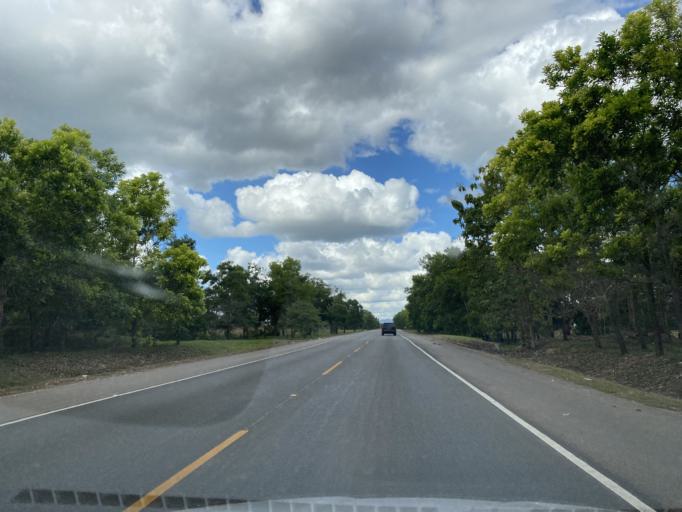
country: DO
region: Santo Domingo
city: Guerra
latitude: 18.6730
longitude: -69.7437
